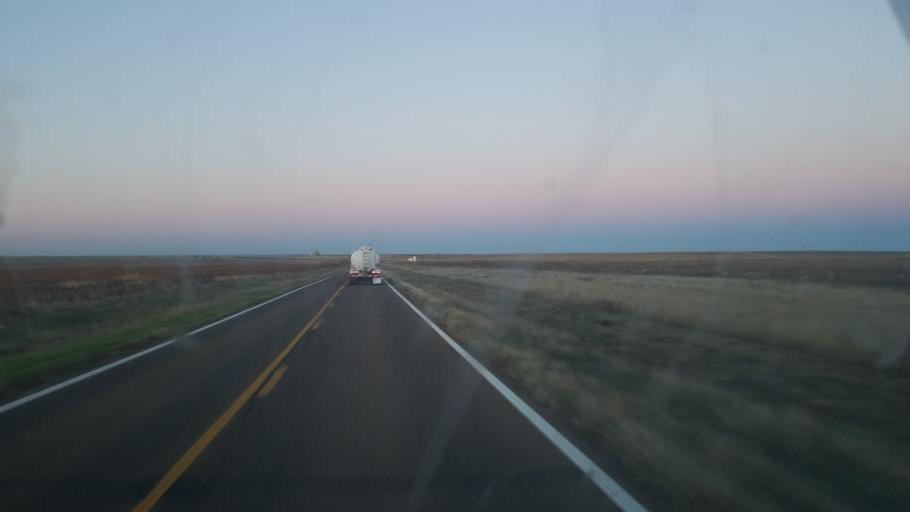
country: US
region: Kansas
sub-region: Wallace County
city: Sharon Springs
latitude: 38.9299
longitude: -101.5481
